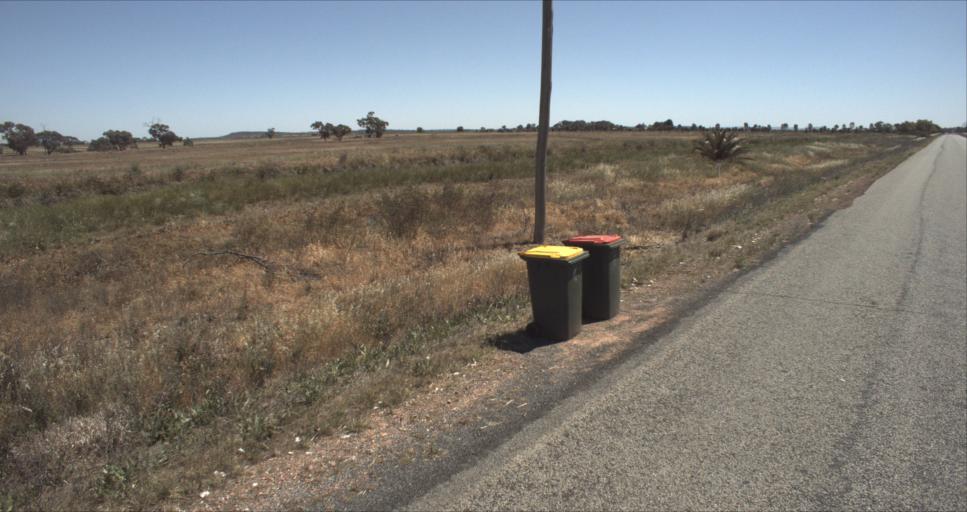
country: AU
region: New South Wales
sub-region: Leeton
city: Leeton
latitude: -34.4474
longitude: 146.2966
